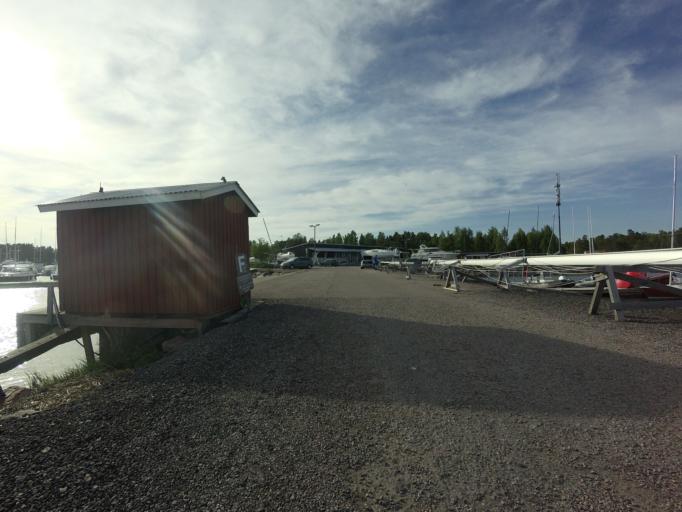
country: FI
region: Uusimaa
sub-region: Helsinki
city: Koukkuniemi
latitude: 60.1429
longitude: 24.7388
